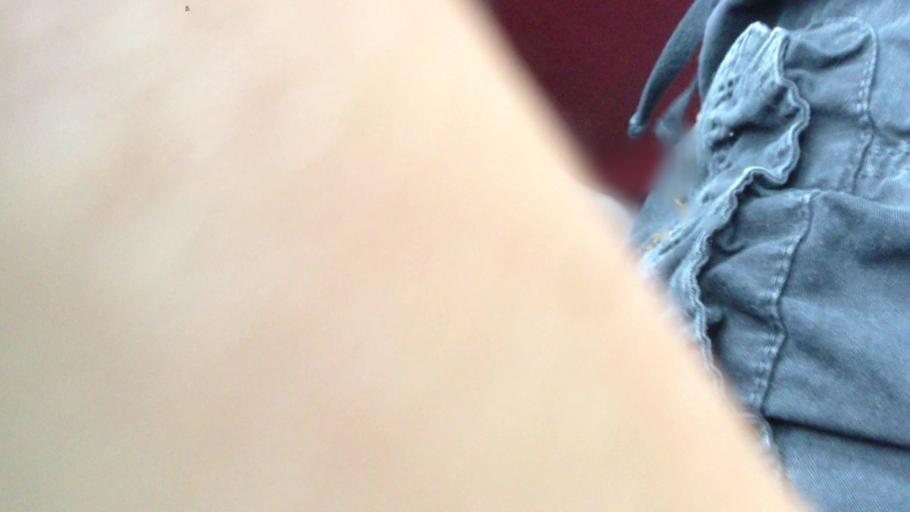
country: US
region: New York
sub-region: Dutchess County
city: Red Hook
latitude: 41.9778
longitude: -73.9198
